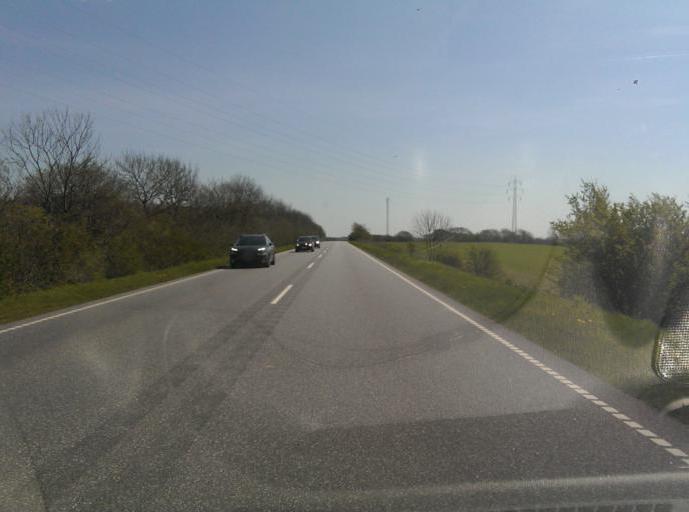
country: DK
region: South Denmark
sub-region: Esbjerg Kommune
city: Bramming
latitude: 55.4231
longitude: 8.6895
